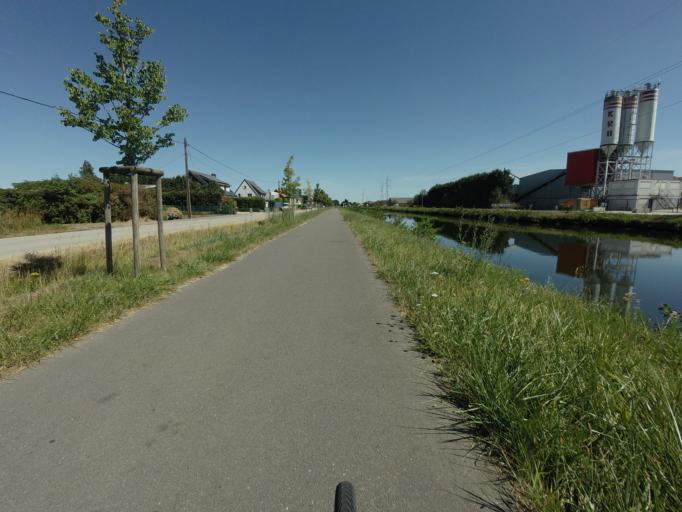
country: BE
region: Flanders
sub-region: Provincie Antwerpen
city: Rijkevorsel
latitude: 51.3329
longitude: 4.7358
